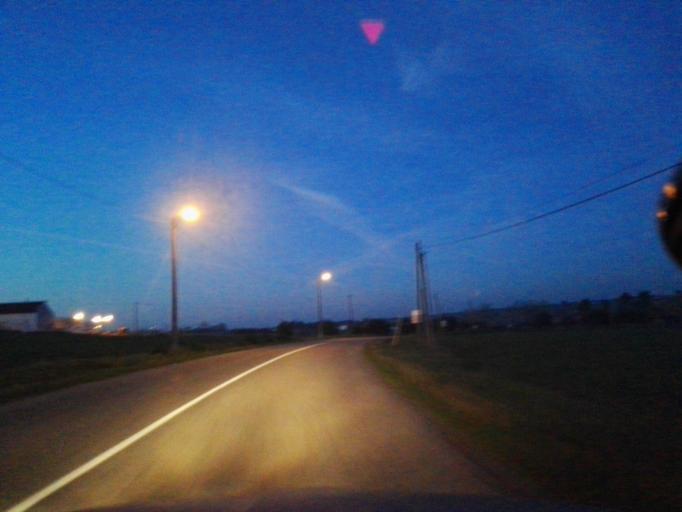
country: PT
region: Evora
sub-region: Arraiolos
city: Arraiolos
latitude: 38.8311
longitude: -7.8354
